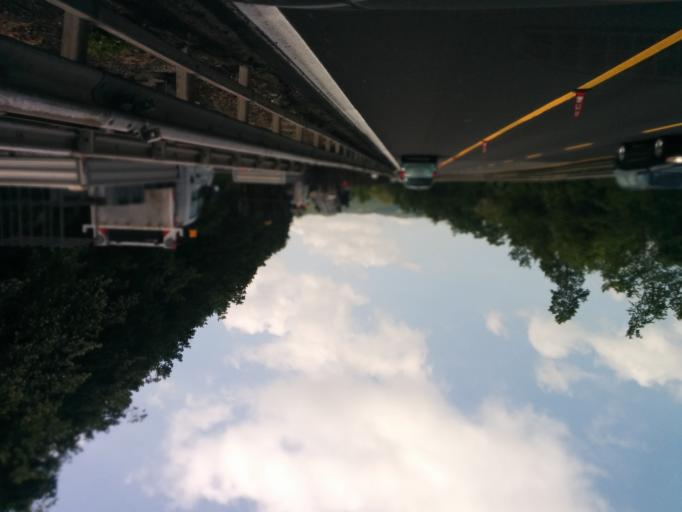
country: IT
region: Emilia-Romagna
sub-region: Provincia di Bologna
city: San Benedetto Val di Sambro
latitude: 44.1670
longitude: 11.2093
